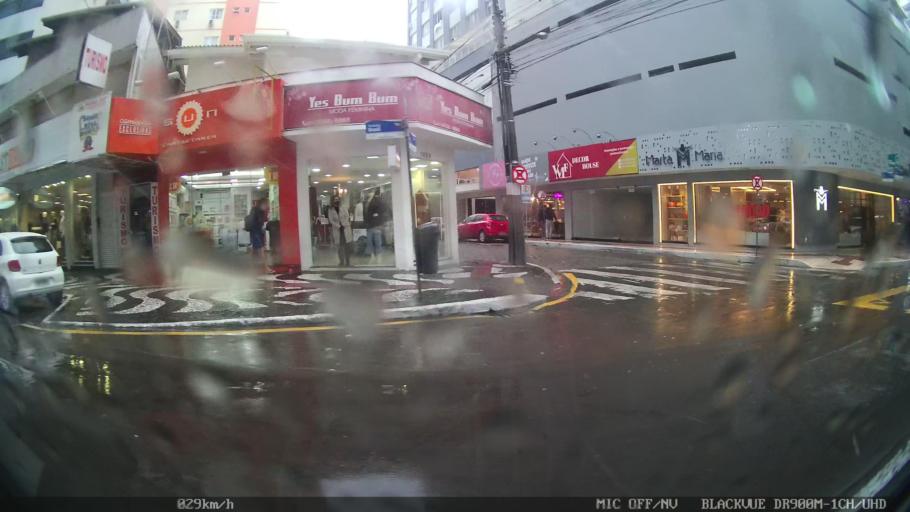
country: BR
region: Santa Catarina
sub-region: Balneario Camboriu
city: Balneario Camboriu
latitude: -26.9849
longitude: -48.6354
